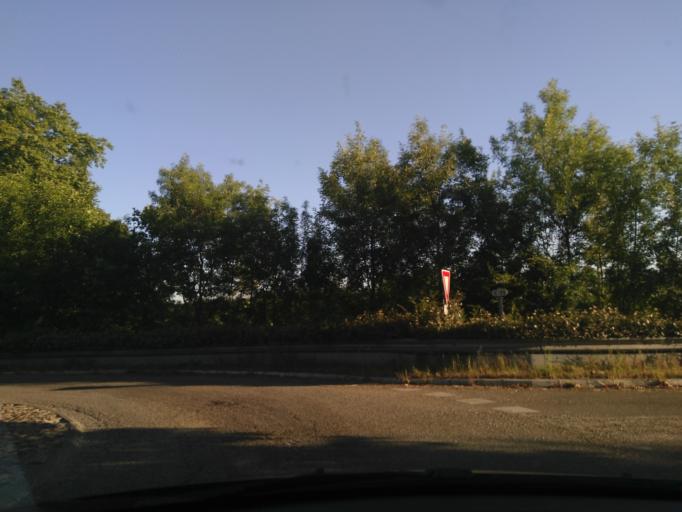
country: FR
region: Midi-Pyrenees
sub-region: Departement du Gers
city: Valence-sur-Baise
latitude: 43.8854
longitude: 0.3794
